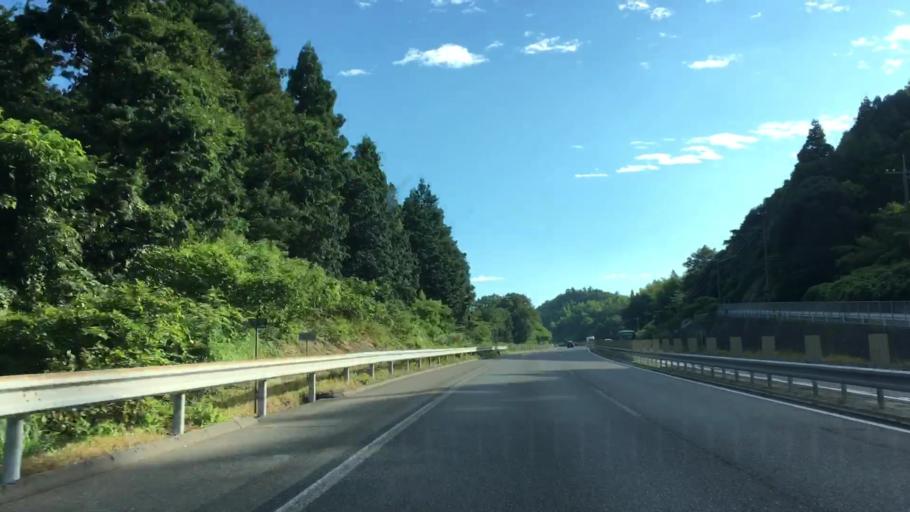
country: JP
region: Yamaguchi
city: Iwakuni
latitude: 34.1362
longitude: 132.1165
